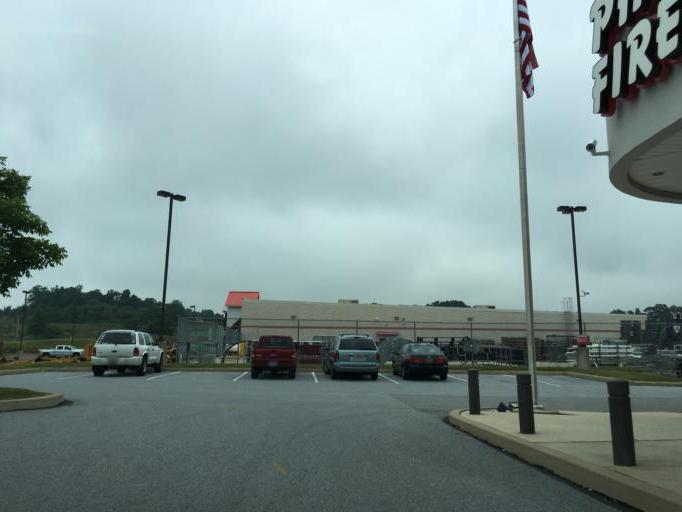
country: US
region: Pennsylvania
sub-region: York County
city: Shrewsbury
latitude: 39.7710
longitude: -76.6615
